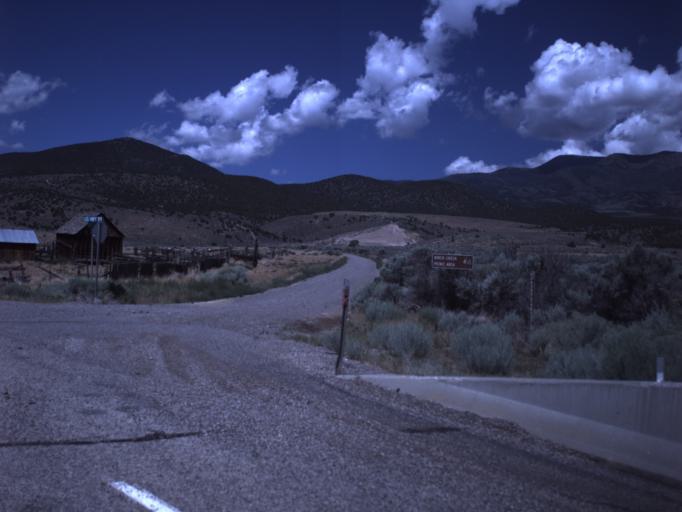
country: US
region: Utah
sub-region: Piute County
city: Junction
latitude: 38.1508
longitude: -112.2915
